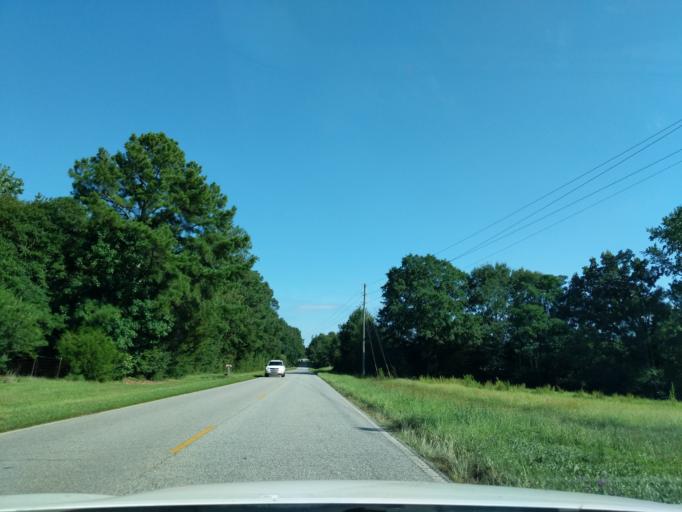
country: US
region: Georgia
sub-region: Oglethorpe County
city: Lexington
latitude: 33.9348
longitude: -83.0475
